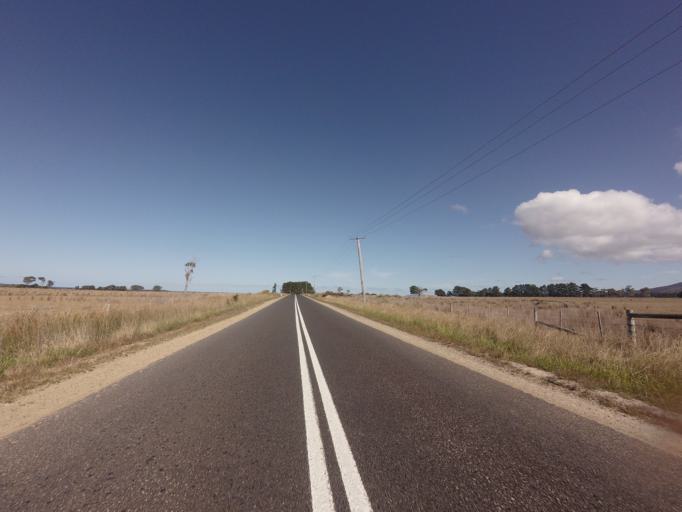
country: AU
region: Tasmania
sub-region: Break O'Day
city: St Helens
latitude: -41.7452
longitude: 148.2745
